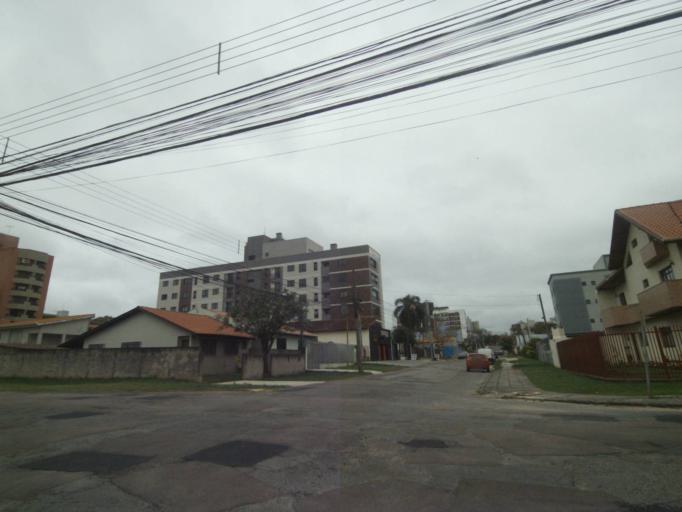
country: BR
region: Parana
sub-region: Curitiba
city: Curitiba
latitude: -25.4722
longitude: -49.2845
